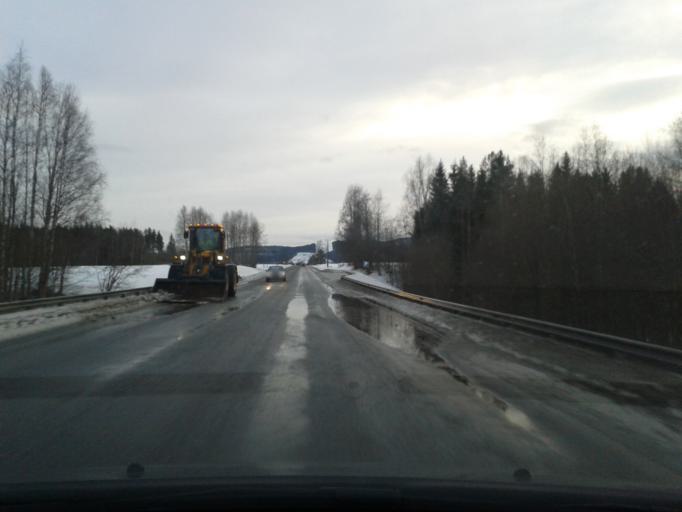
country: SE
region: Vaesternorrland
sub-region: Solleftea Kommun
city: Solleftea
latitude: 63.2525
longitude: 17.2151
